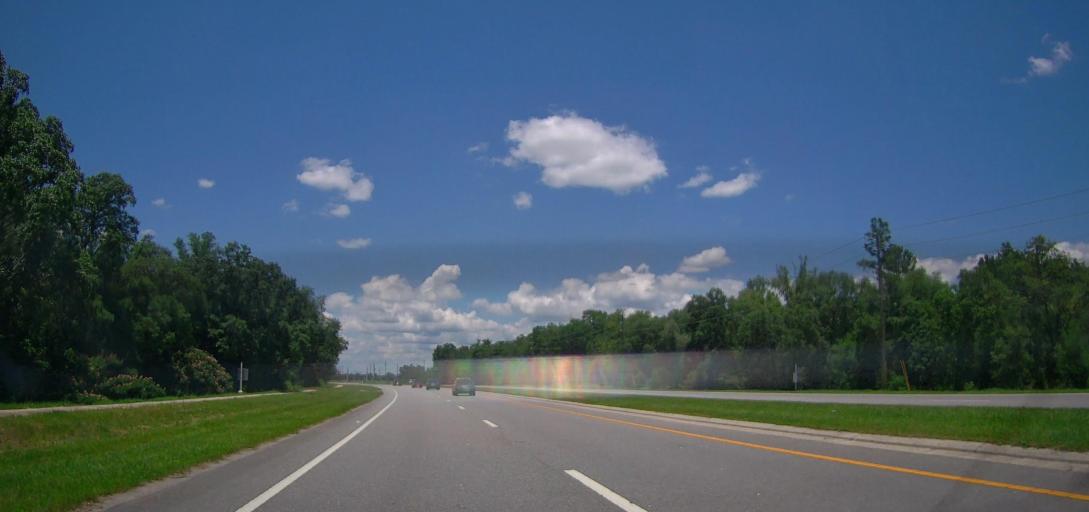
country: US
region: Florida
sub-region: Marion County
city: Silver Springs Shores
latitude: 29.0599
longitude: -82.0167
